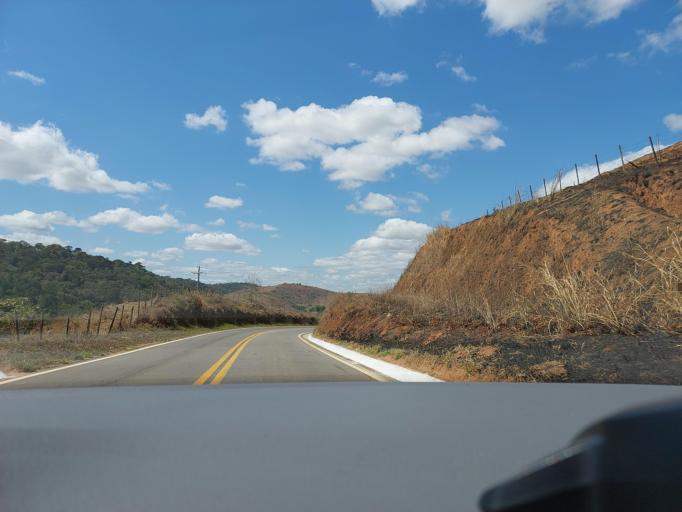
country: BR
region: Minas Gerais
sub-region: Muriae
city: Muriae
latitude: -21.1034
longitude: -42.4627
